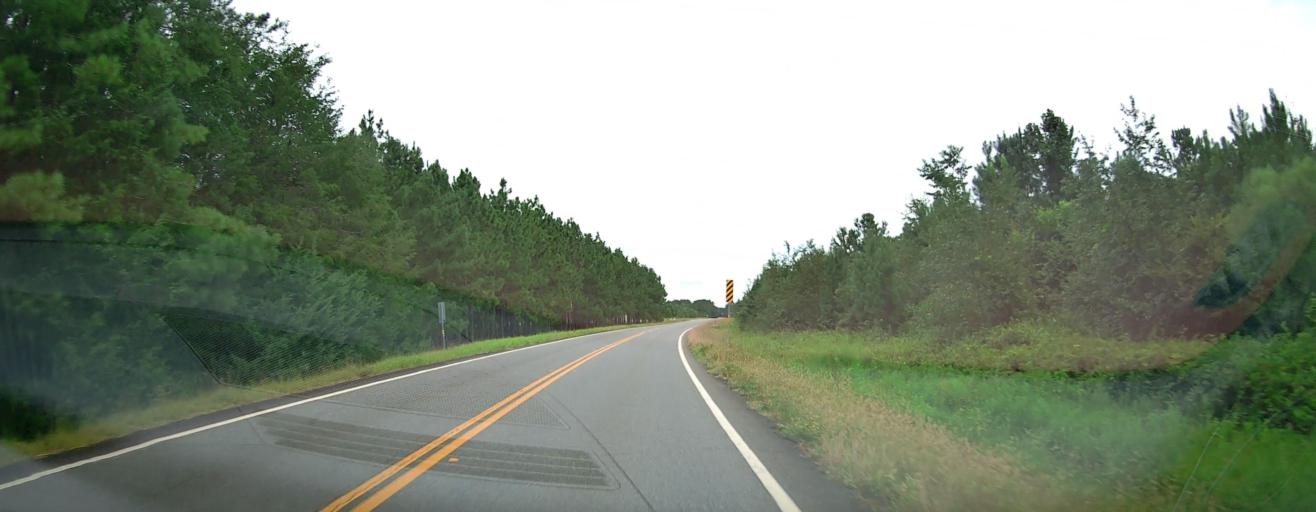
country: US
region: Georgia
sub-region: Marion County
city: Buena Vista
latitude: 32.2665
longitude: -84.4299
